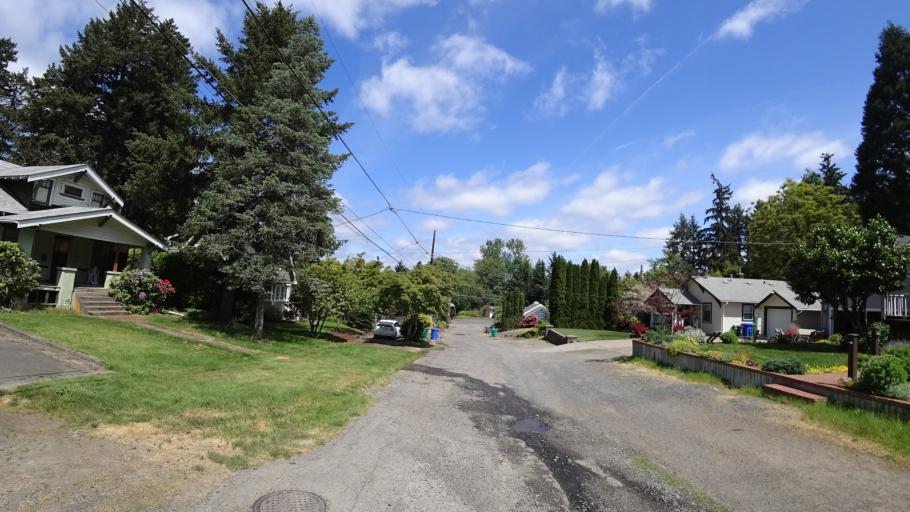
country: US
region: Oregon
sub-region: Washington County
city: Garden Home-Whitford
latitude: 45.4656
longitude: -122.7193
